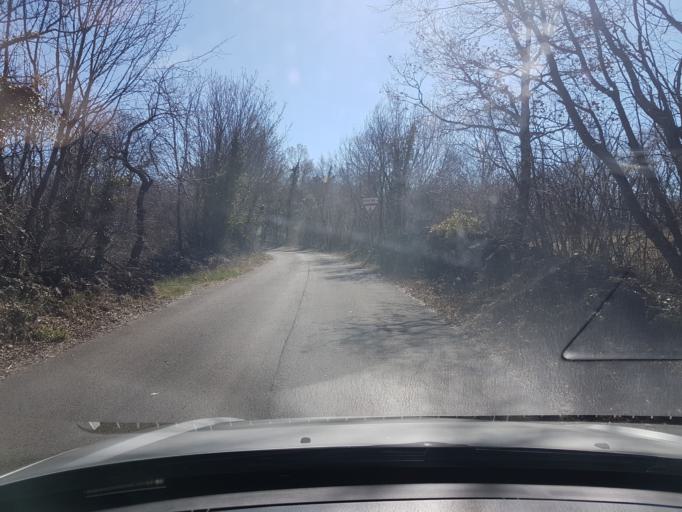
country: IT
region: Friuli Venezia Giulia
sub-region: Provincia di Trieste
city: Sistiana-Visogliano
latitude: 45.7863
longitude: 13.6536
